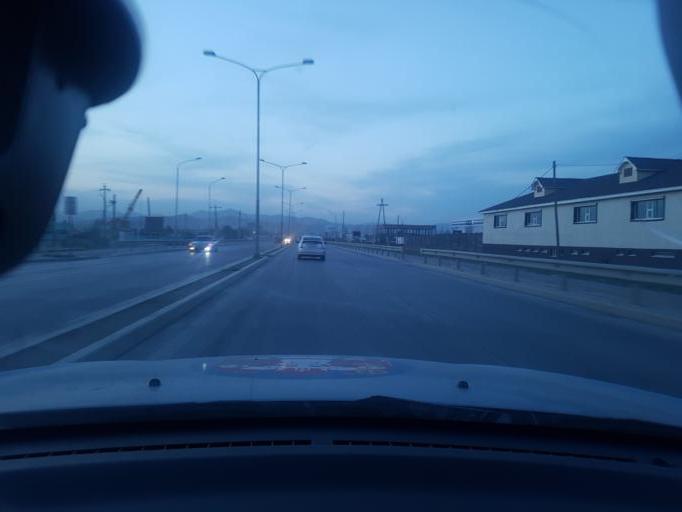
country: MN
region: Ulaanbaatar
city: Ulaanbaatar
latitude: 47.8967
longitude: 106.7856
